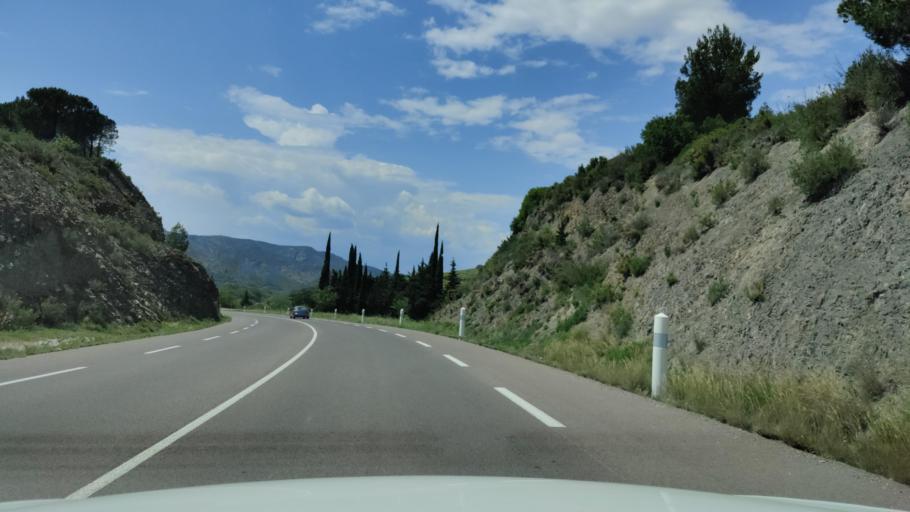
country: FR
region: Languedoc-Roussillon
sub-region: Departement des Pyrenees-Orientales
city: Baixas
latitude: 42.7780
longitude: 2.7718
